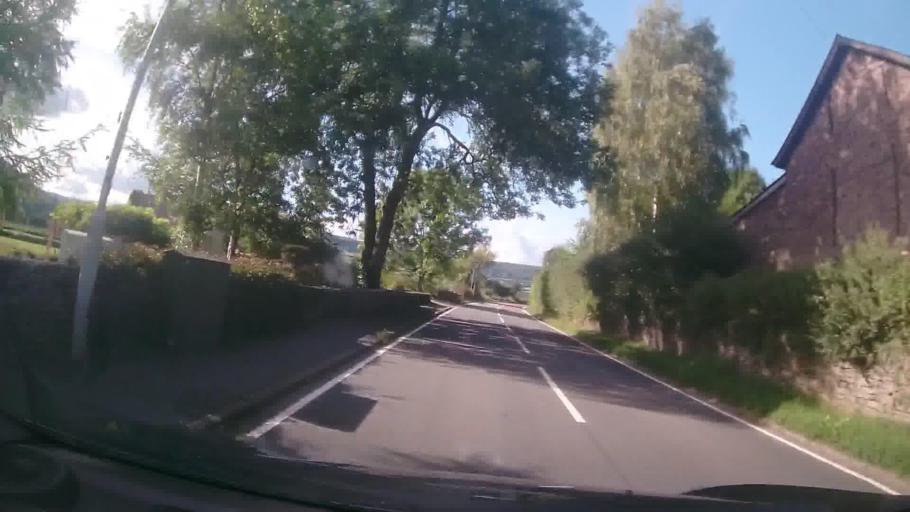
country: GB
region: Wales
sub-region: Blaenau Gwent
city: Brynmawr
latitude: 51.8865
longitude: -3.1857
